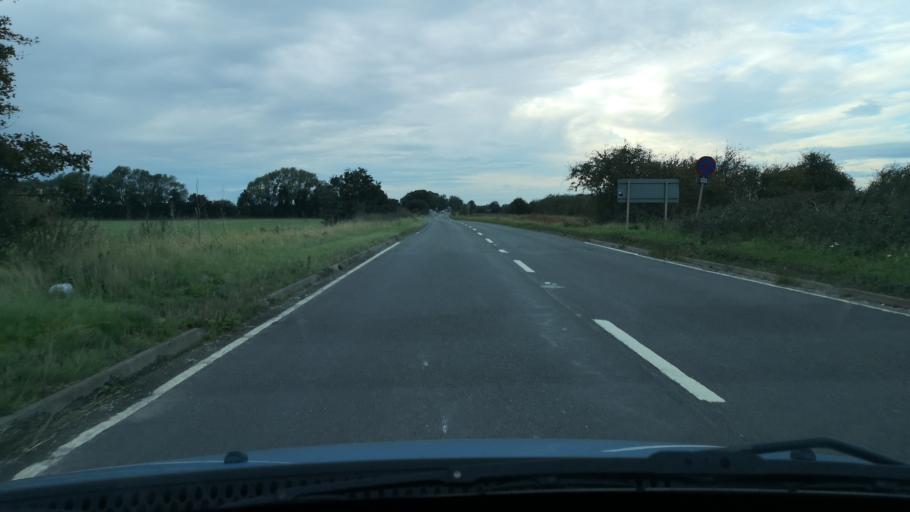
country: GB
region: England
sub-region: North Lincolnshire
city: Crowle
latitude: 53.5822
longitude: -0.8925
